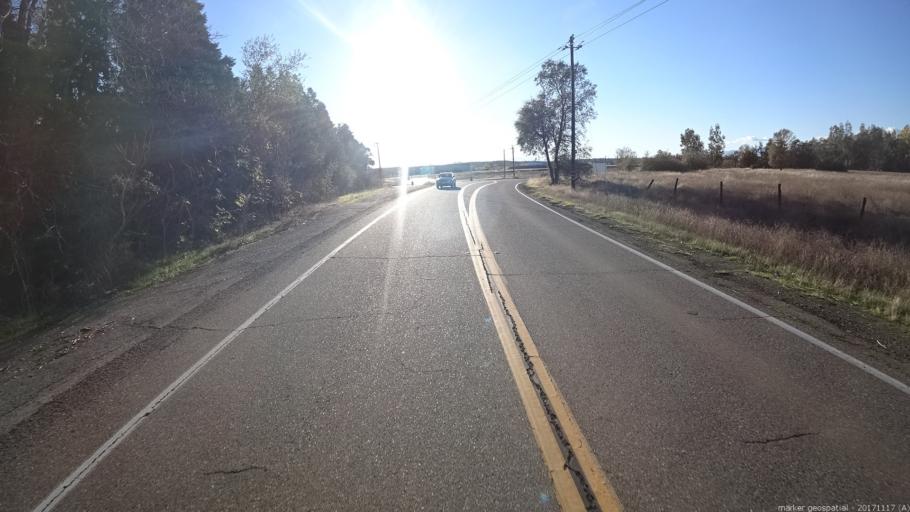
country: US
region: California
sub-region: Shasta County
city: Anderson
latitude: 40.4390
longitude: -122.2692
